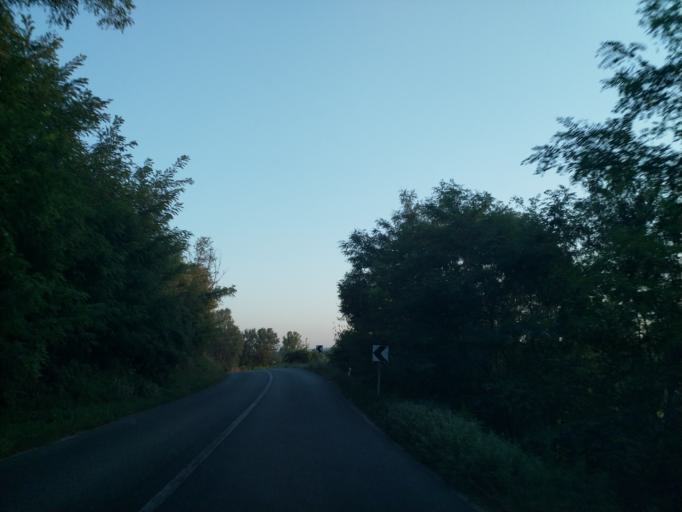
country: RS
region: Central Serbia
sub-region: Rasinski Okrug
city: Krusevac
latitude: 43.6100
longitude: 21.2093
